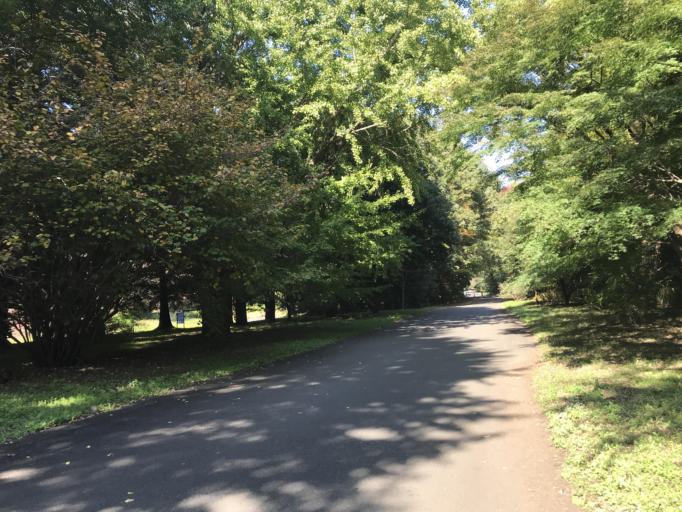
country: JP
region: Tokyo
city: Hino
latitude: 35.7132
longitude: 139.3989
